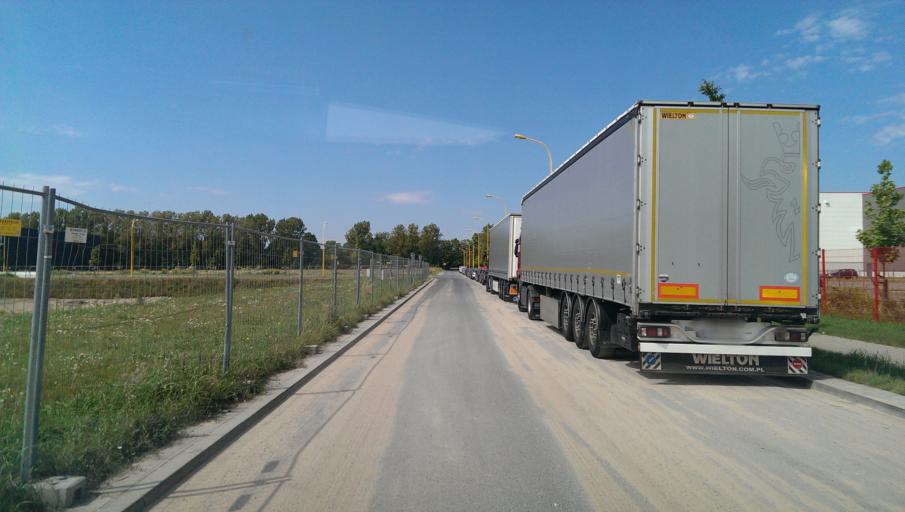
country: DE
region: Brandenburg
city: Grossbeeren
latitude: 52.3759
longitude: 13.3278
